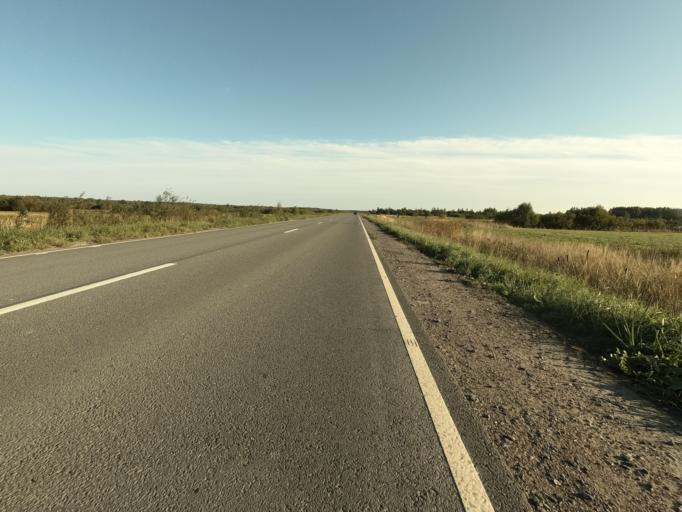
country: RU
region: St.-Petersburg
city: Sapernyy
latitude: 59.7495
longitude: 30.6396
